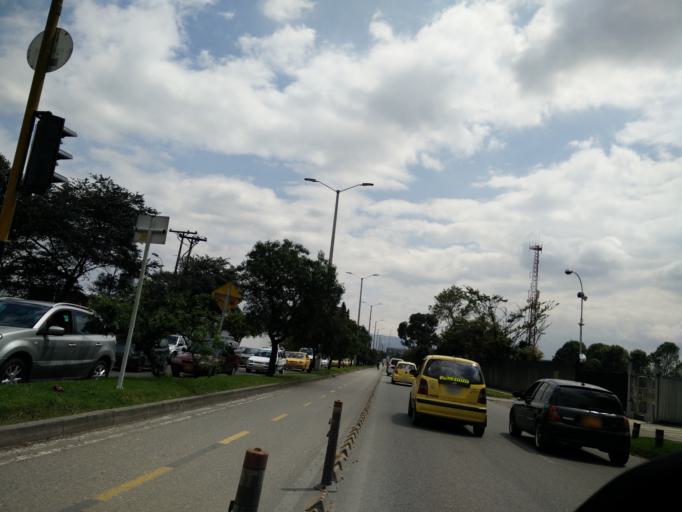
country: CO
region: Bogota D.C.
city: Bogota
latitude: 4.6354
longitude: -74.1009
